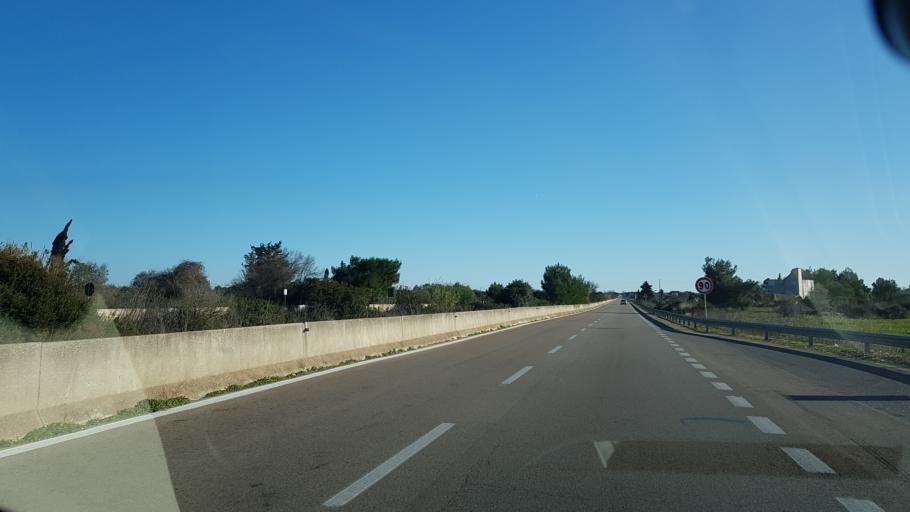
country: IT
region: Apulia
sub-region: Provincia di Lecce
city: Alezio
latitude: 40.0254
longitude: 18.0365
